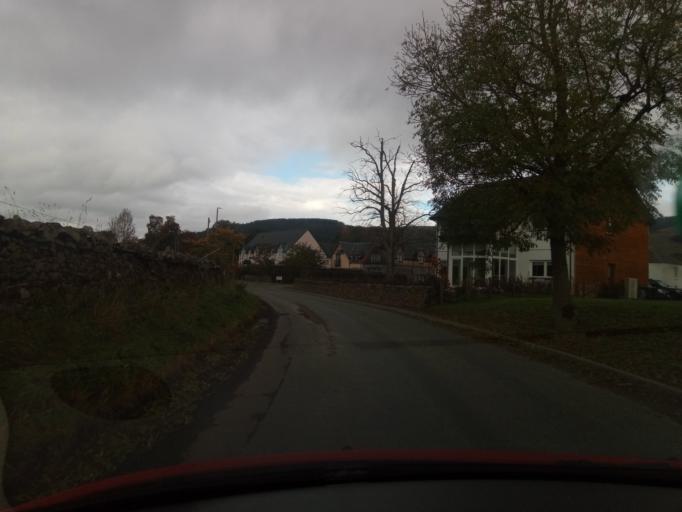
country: GB
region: Scotland
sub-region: The Scottish Borders
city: Innerleithen
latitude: 55.6390
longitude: -3.1102
